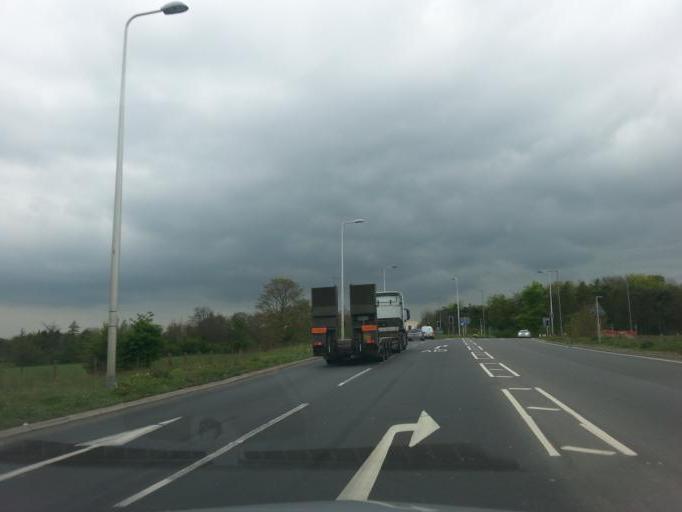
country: GB
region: England
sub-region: Peterborough
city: Wansford
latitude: 52.5847
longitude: -0.4107
